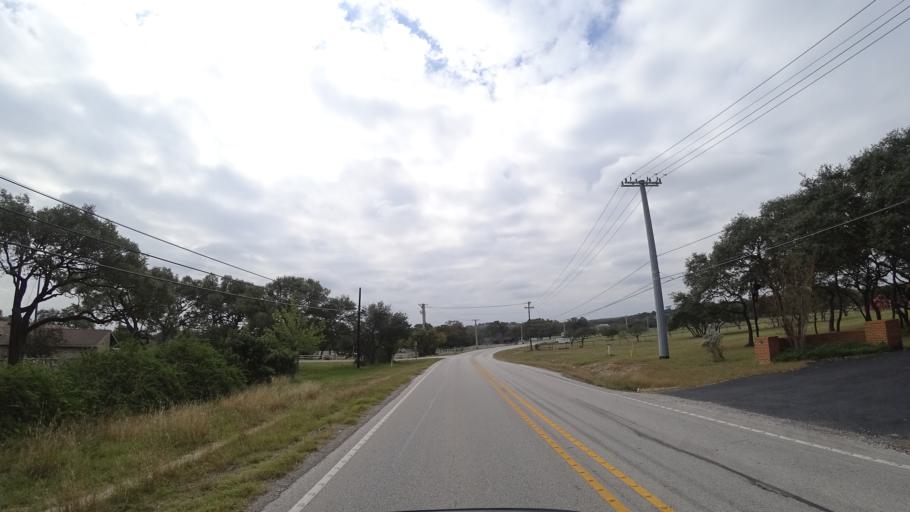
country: US
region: Texas
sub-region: Travis County
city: Shady Hollow
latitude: 30.2111
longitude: -97.8985
